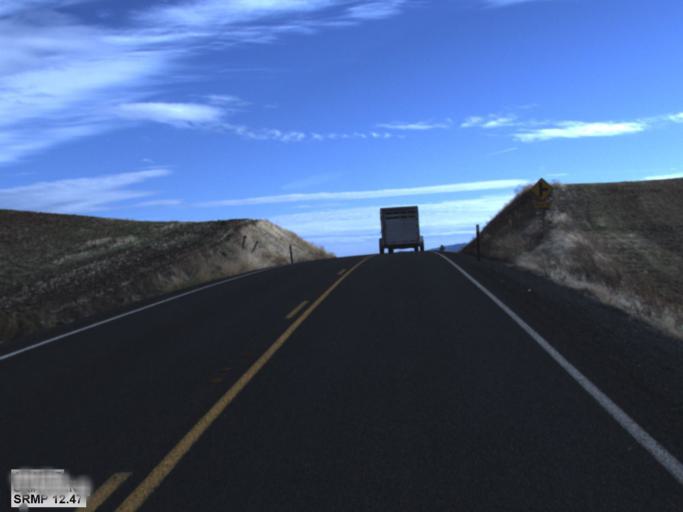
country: US
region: Washington
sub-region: Whitman County
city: Pullman
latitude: 46.9343
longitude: -117.1402
